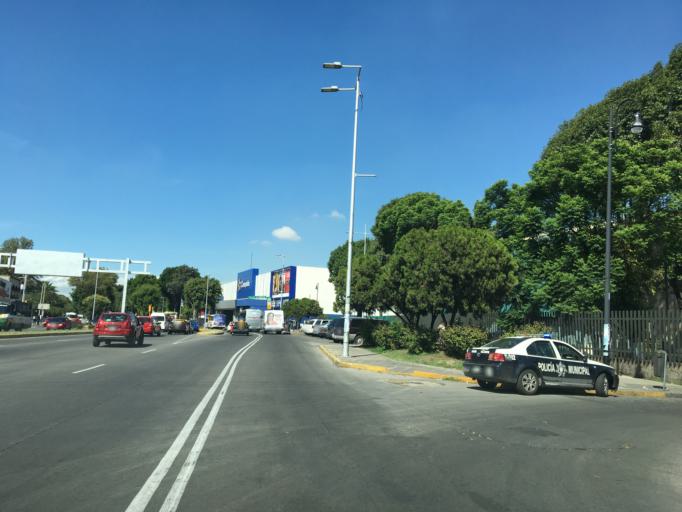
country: MX
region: Puebla
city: Puebla
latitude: 19.0399
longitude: -98.1954
